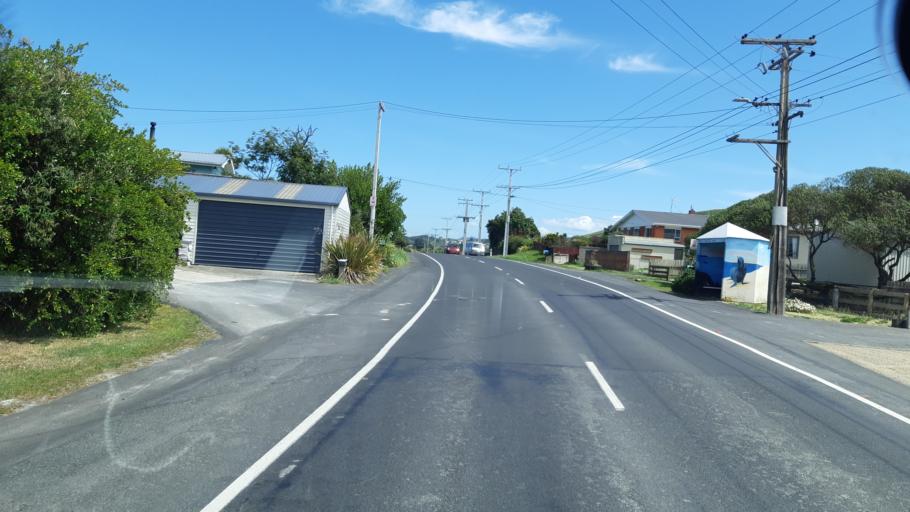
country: NZ
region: Otago
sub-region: Dunedin City
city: Dunedin
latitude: -45.9346
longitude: 170.3710
